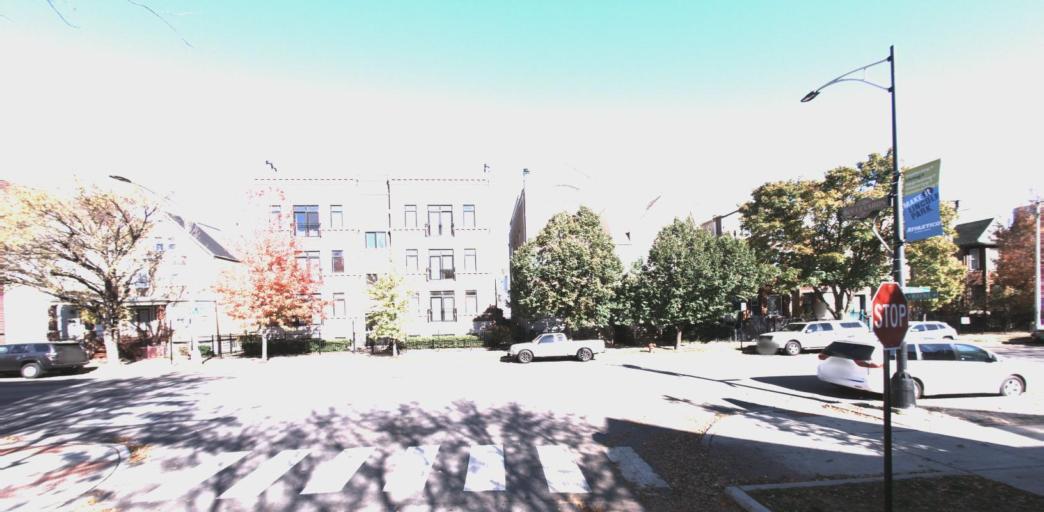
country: US
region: Illinois
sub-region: Cook County
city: Chicago
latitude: 41.9324
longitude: -87.6623
